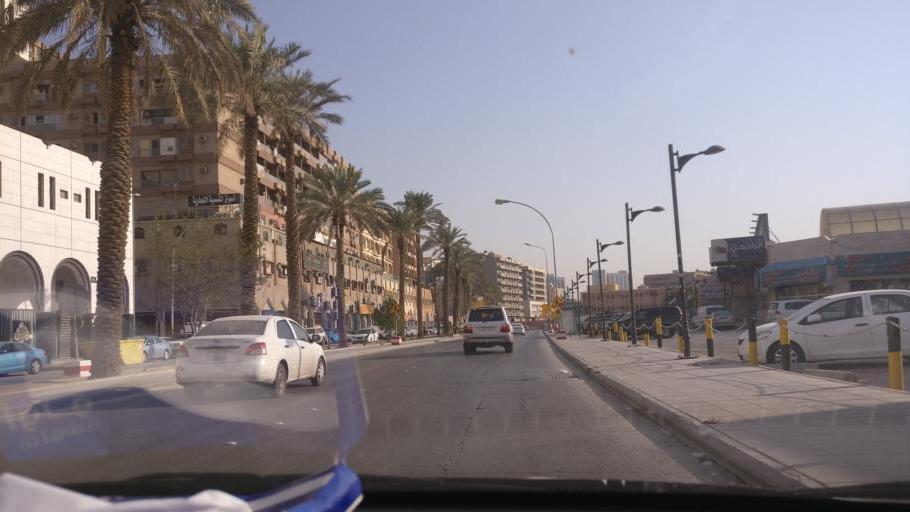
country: SA
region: Ar Riyad
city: Riyadh
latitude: 24.6421
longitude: 46.7141
